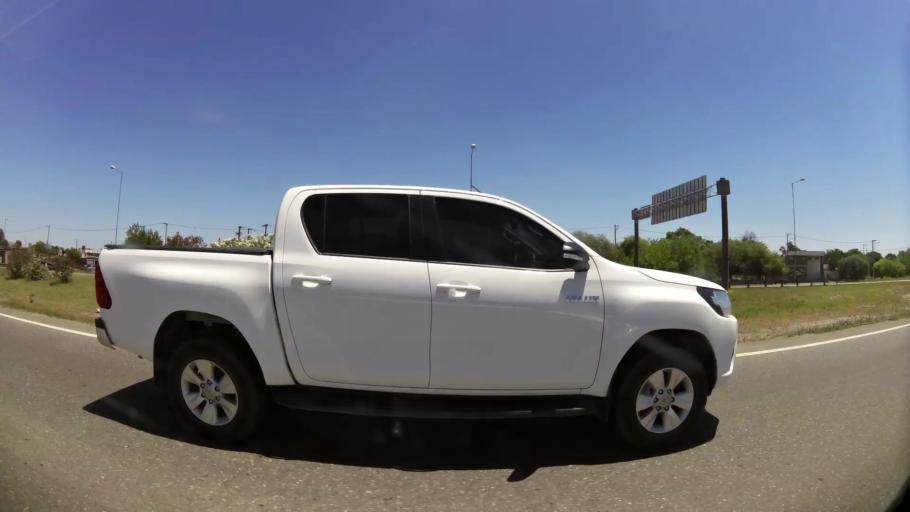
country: AR
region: Cordoba
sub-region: Departamento de Capital
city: Cordoba
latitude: -31.4354
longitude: -64.1158
